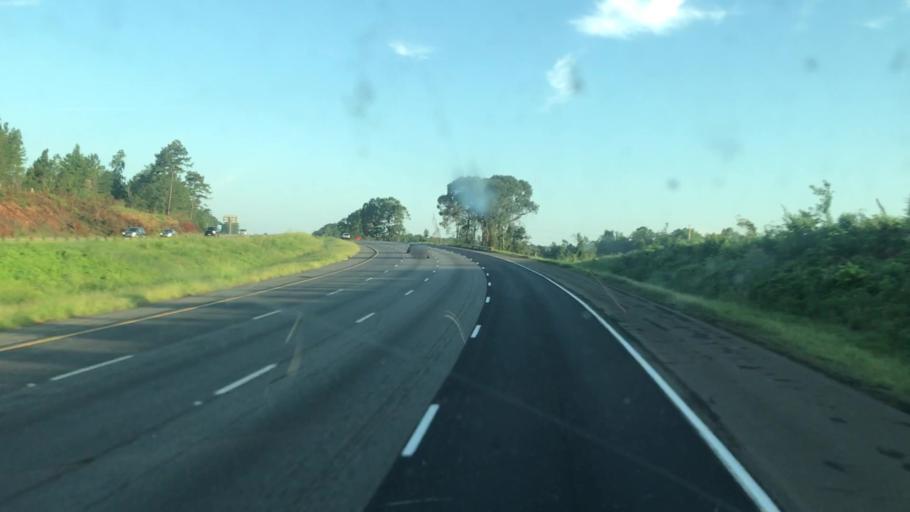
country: US
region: Georgia
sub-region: Monroe County
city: Forsyth
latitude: 32.9832
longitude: -83.8327
